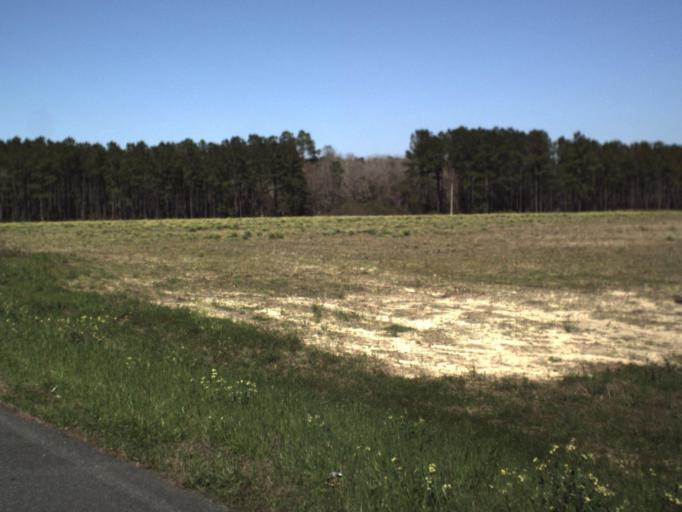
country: US
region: Florida
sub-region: Gulf County
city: Wewahitchka
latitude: 30.2346
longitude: -85.2079
